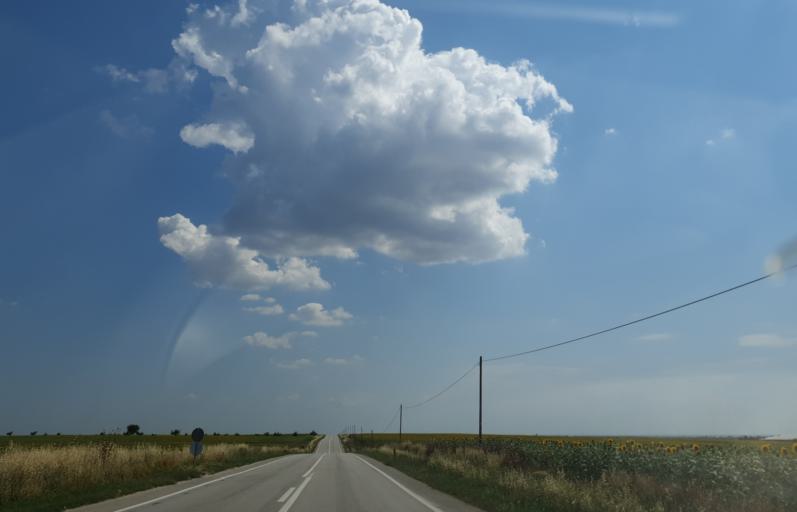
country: TR
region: Kirklareli
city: Buyukkaristiran
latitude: 41.4318
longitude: 27.5824
